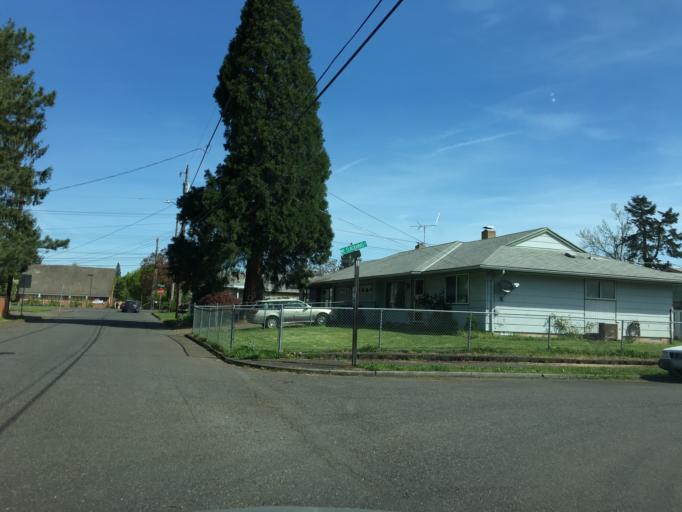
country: US
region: Oregon
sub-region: Multnomah County
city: Lents
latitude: 45.5327
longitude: -122.5338
